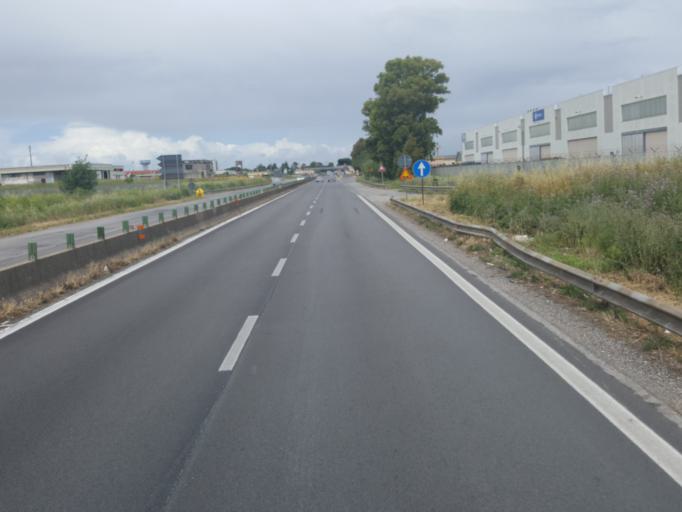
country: IT
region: Latium
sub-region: Provincia di Latina
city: Aprilia
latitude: 41.5726
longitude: 12.6629
